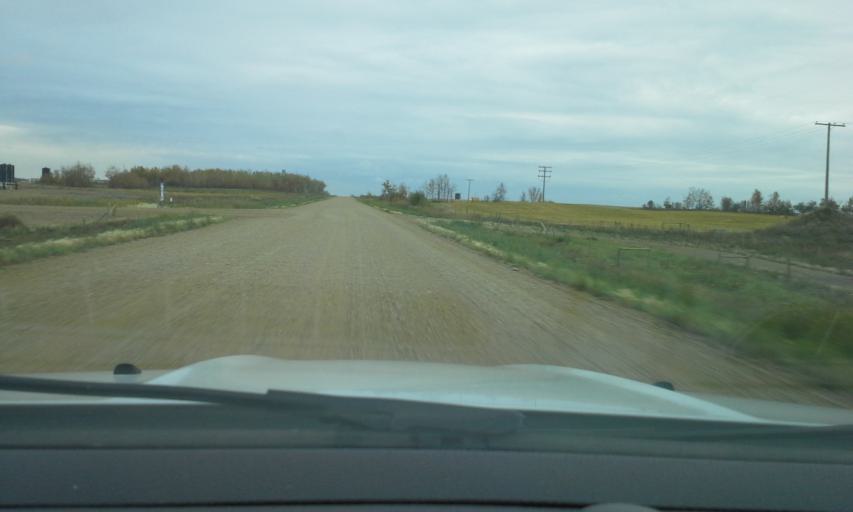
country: CA
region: Saskatchewan
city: Lloydminster
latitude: 53.2824
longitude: -109.8084
